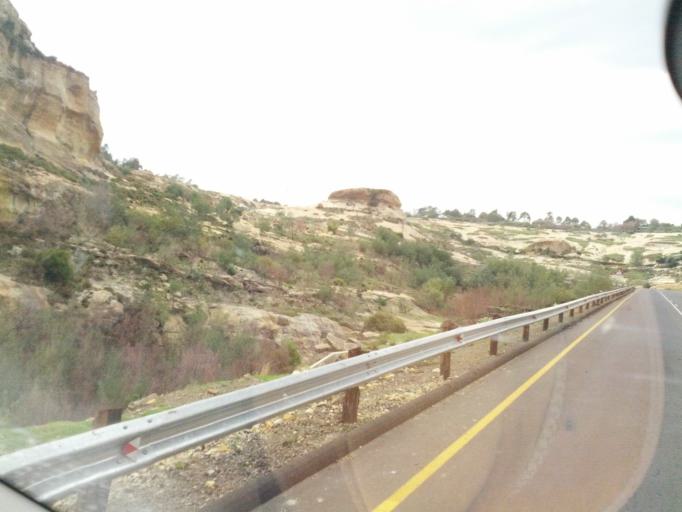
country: LS
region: Maseru
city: Nako
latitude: -29.4828
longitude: 27.7412
